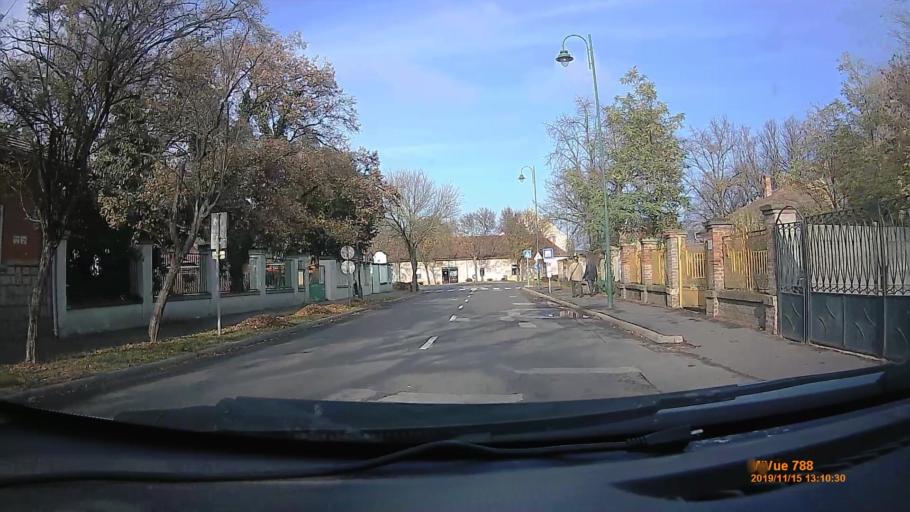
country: HU
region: Bekes
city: Gyula
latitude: 46.6441
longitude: 21.2805
